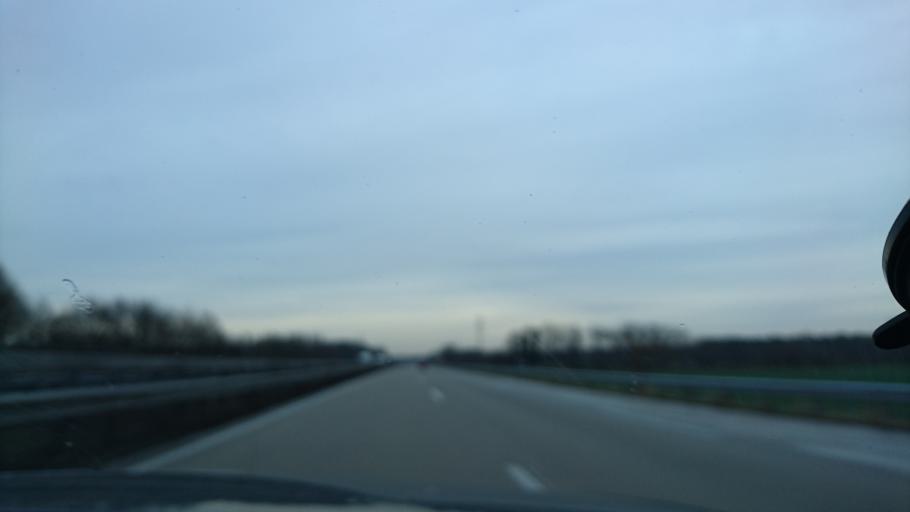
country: DE
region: Lower Saxony
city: Isterberg
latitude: 52.3363
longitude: 7.1121
